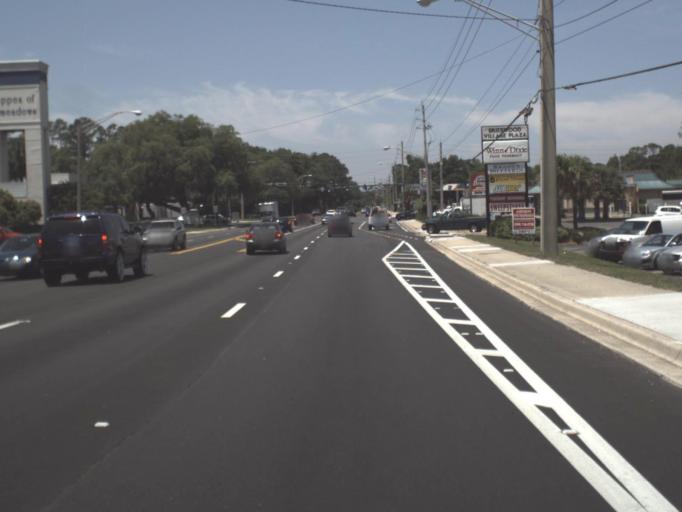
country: US
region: Florida
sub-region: Saint Johns County
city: Fruit Cove
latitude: 30.2208
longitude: -81.5911
